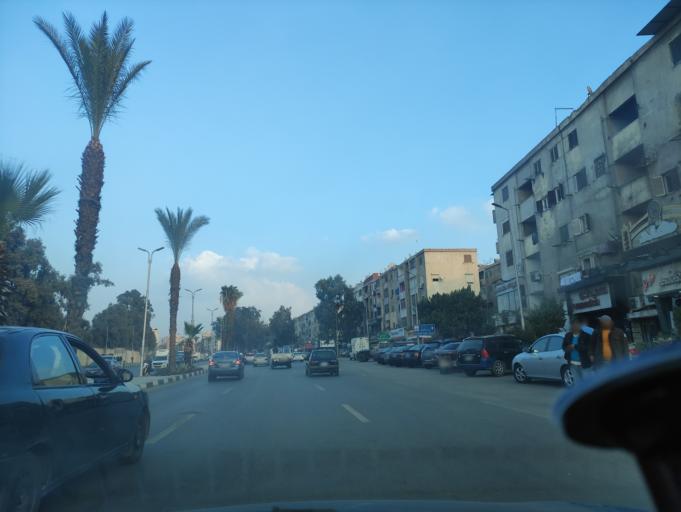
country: EG
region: Muhafazat al Qahirah
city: Cairo
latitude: 30.0501
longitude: 31.3161
